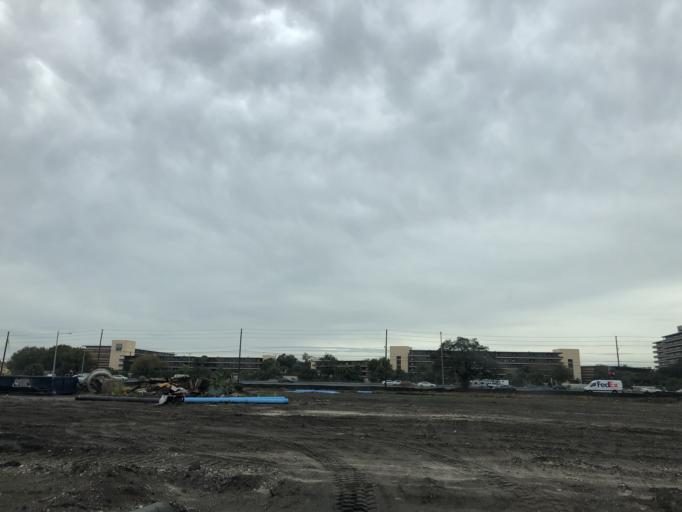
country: US
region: Florida
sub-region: Orange County
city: Doctor Phillips
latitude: 28.4327
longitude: -81.4761
